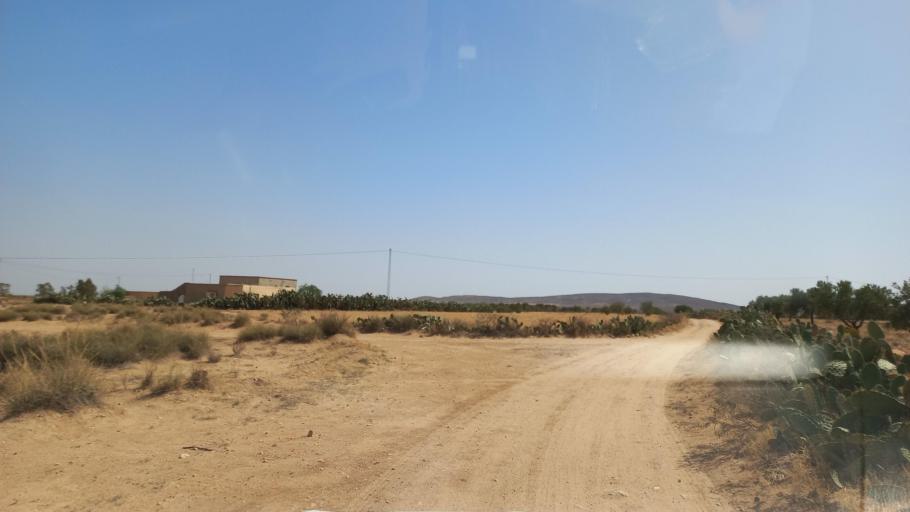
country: TN
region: Al Qasrayn
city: Kasserine
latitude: 35.2200
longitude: 9.0362
